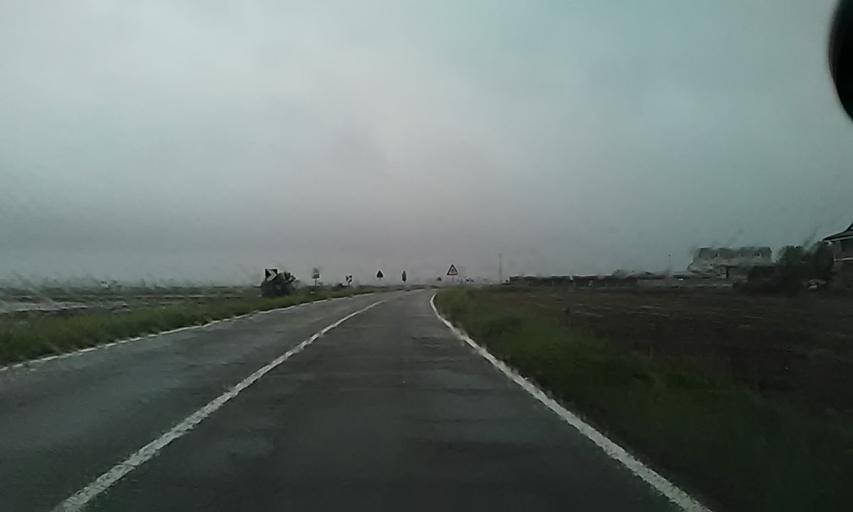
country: IT
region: Piedmont
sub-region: Provincia di Vercelli
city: Albano Vercellese
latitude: 45.4257
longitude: 8.3768
